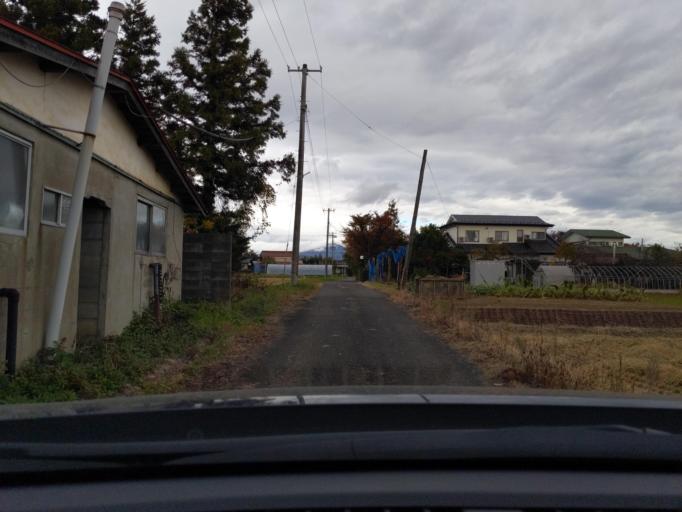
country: JP
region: Fukushima
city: Koriyama
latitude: 37.4088
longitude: 140.3036
